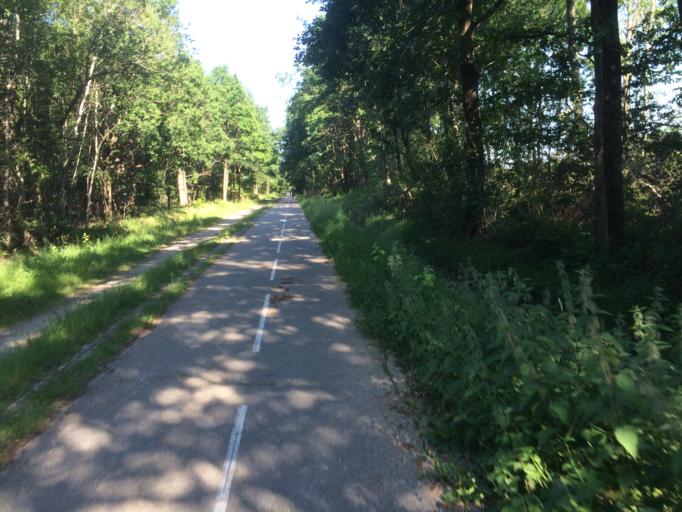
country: FR
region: Ile-de-France
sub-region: Departement du Val-de-Marne
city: Sucy-en-Brie
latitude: 48.7482
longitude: 2.5477
